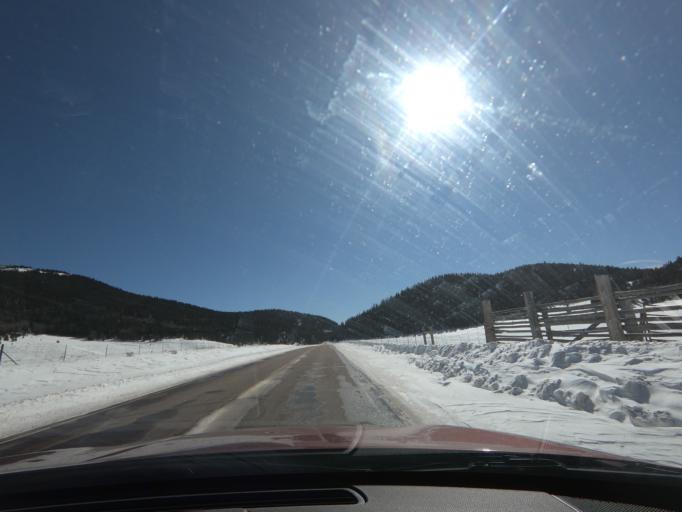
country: US
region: Colorado
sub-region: Teller County
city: Cripple Creek
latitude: 38.7587
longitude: -105.1091
